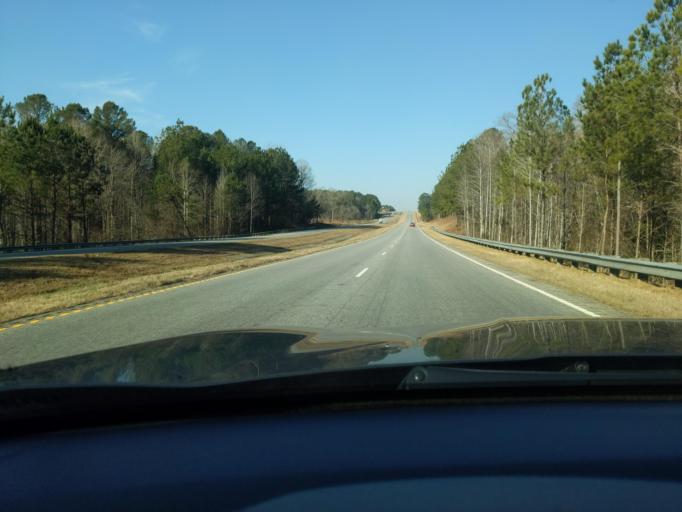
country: US
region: South Carolina
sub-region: Abbeville County
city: Abbeville
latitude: 34.1837
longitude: -82.3098
